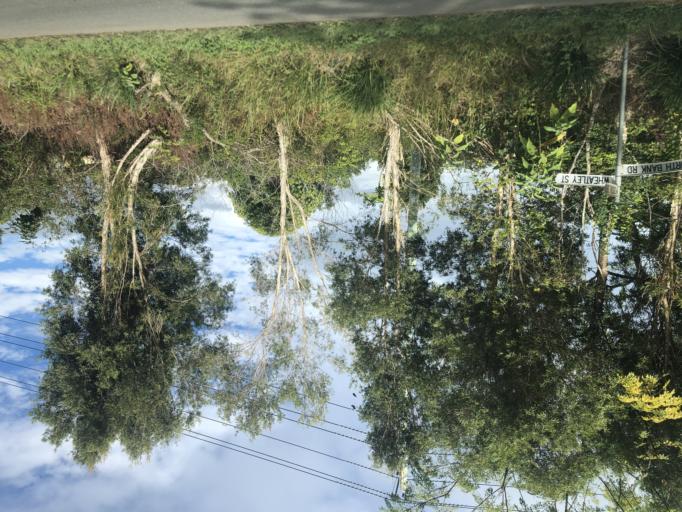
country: AU
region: New South Wales
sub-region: Bellingen
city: Bellingen
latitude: -30.4470
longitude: 152.9041
